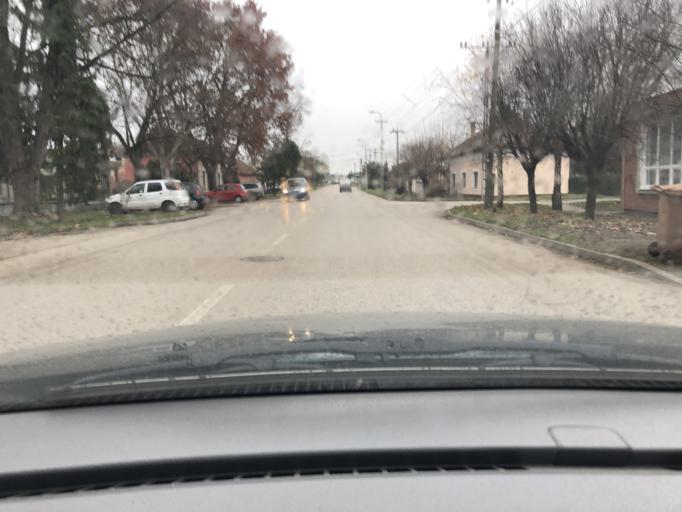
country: HU
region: Csongrad
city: Csongrad
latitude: 46.7027
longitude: 20.1471
